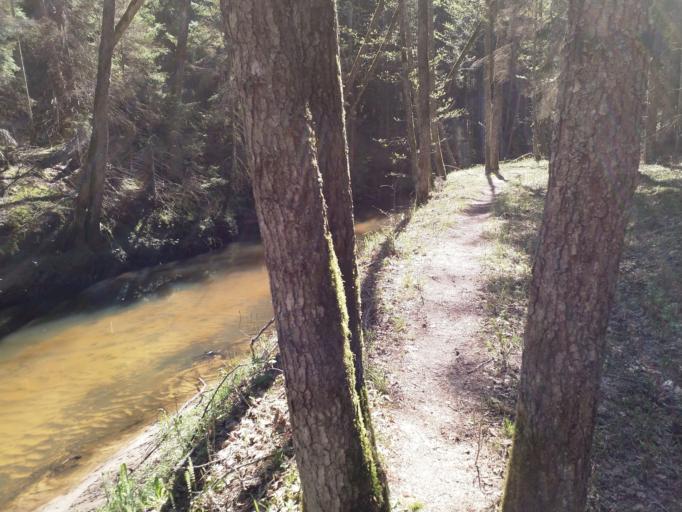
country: LV
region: Pavilostas
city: Pavilosta
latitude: 56.9584
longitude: 21.3523
